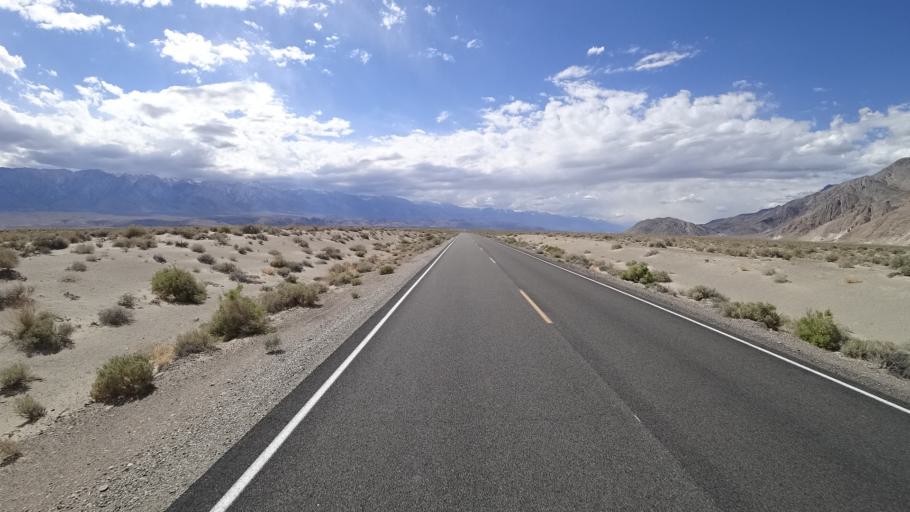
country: US
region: California
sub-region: Inyo County
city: Lone Pine
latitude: 36.5556
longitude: -117.9596
